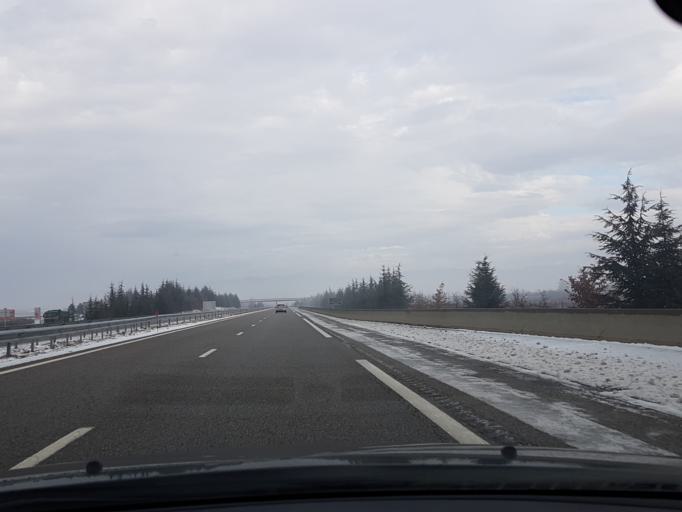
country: FR
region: Provence-Alpes-Cote d'Azur
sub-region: Departement des Alpes-de-Haute-Provence
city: Sisteron
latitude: 44.2344
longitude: 5.9163
